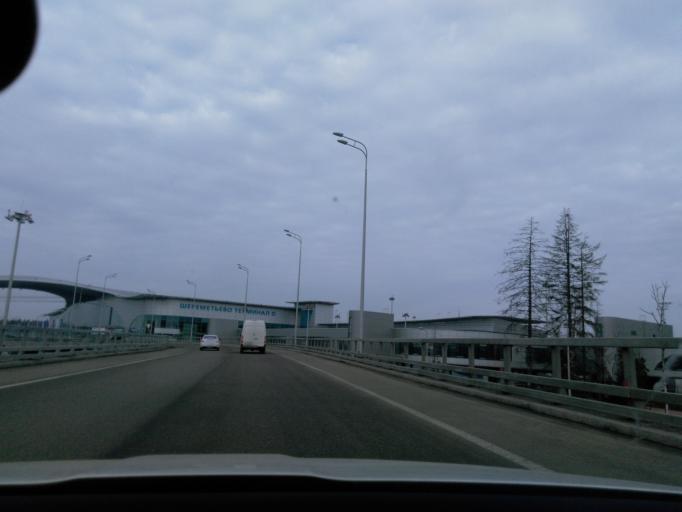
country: RU
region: Moscow
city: Khimki
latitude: 55.9621
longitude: 37.4145
